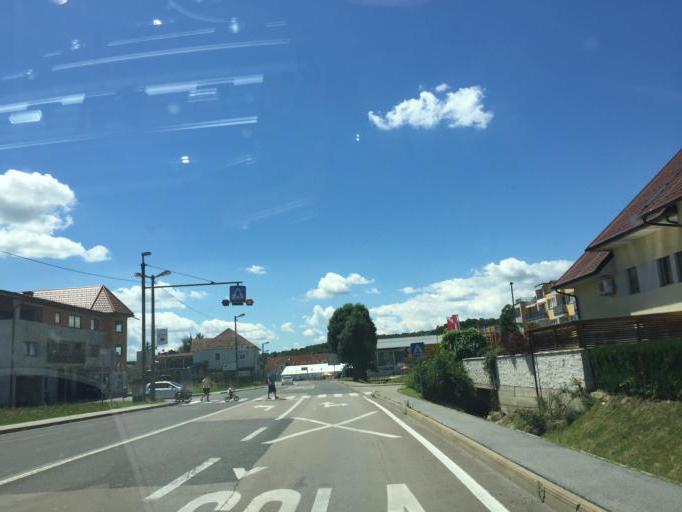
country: SI
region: Benedikt
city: Benedikt
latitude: 46.6091
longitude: 15.8929
